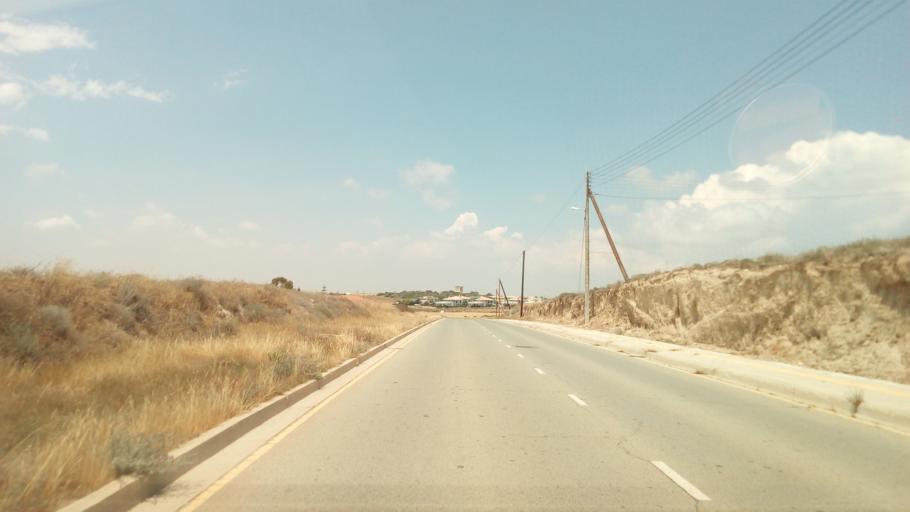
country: CY
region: Larnaka
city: Perivolia
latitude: 34.8256
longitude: 33.6014
